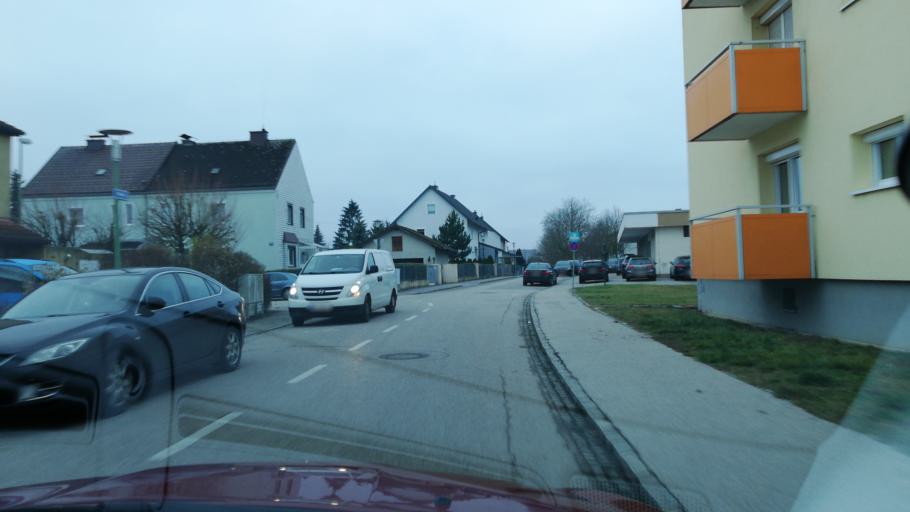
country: AT
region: Upper Austria
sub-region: Wels Stadt
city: Wels
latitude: 48.1686
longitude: 14.0400
